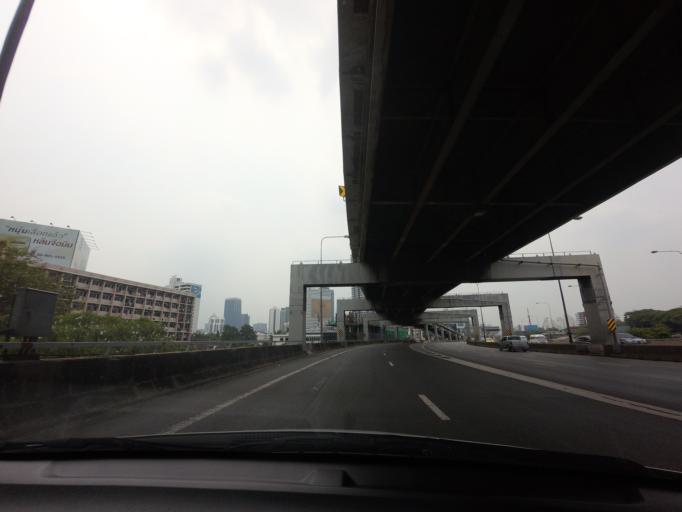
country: TH
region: Bangkok
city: Khlong Toei
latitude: 13.7187
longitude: 100.5532
